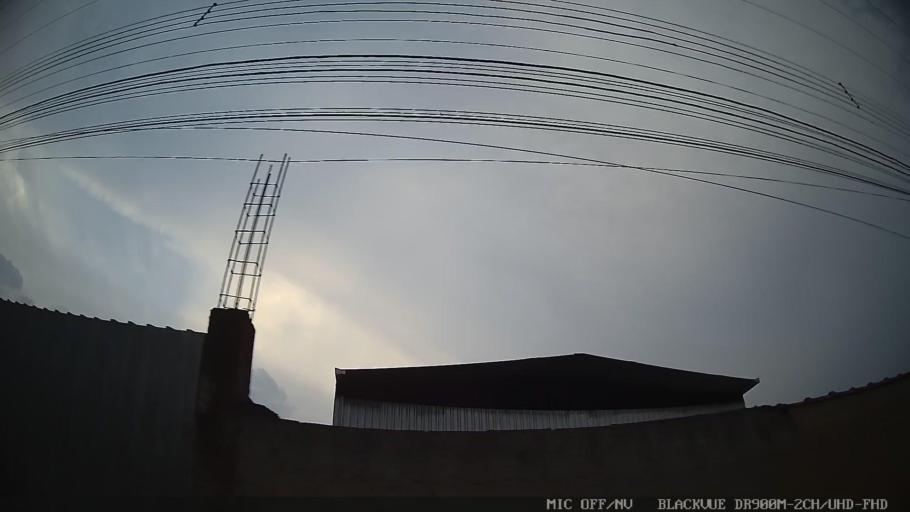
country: BR
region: Sao Paulo
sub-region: Braganca Paulista
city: Braganca Paulista
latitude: -22.9285
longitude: -46.5376
